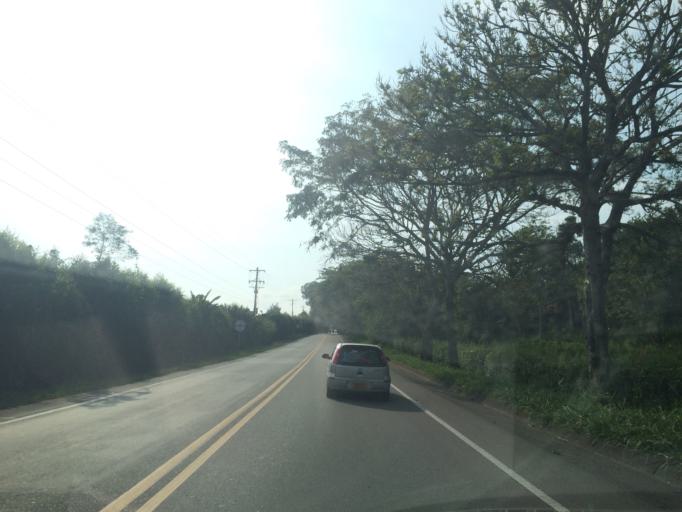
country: CO
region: Quindio
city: La Tebaida
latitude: 4.4480
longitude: -75.8197
